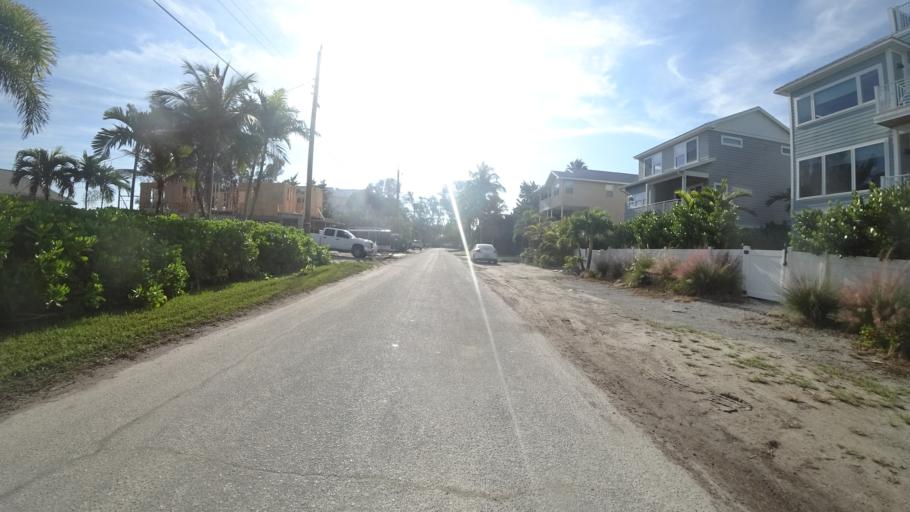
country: US
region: Florida
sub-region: Manatee County
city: Anna Maria
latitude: 27.5364
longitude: -82.7385
